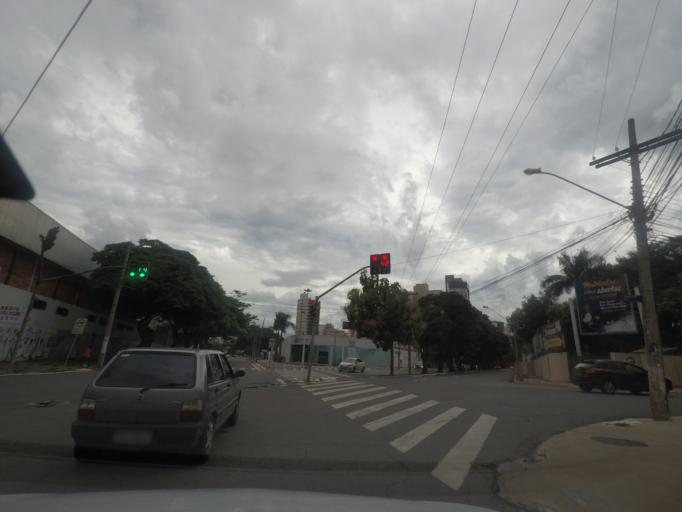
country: BR
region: Goias
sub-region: Goiania
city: Goiania
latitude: -16.6780
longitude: -49.2645
